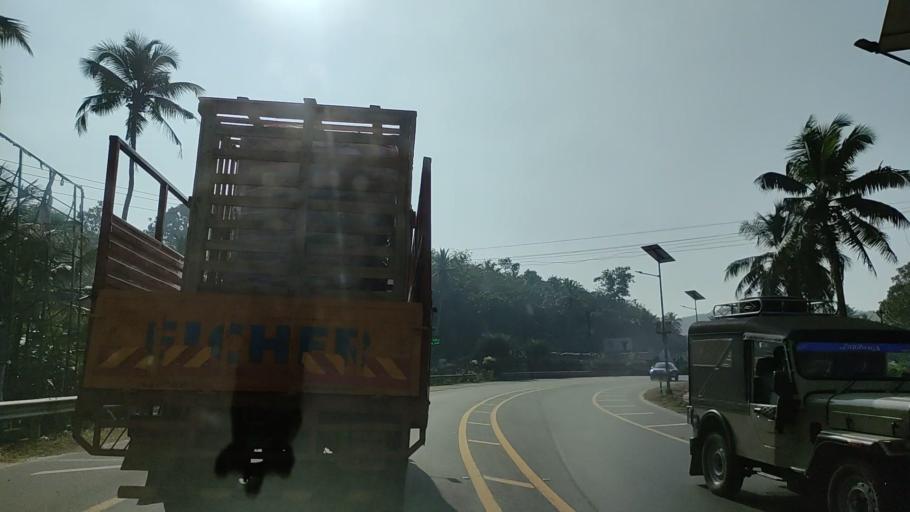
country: IN
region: Kerala
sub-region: Kollam
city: Punalur
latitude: 8.9731
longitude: 76.8283
